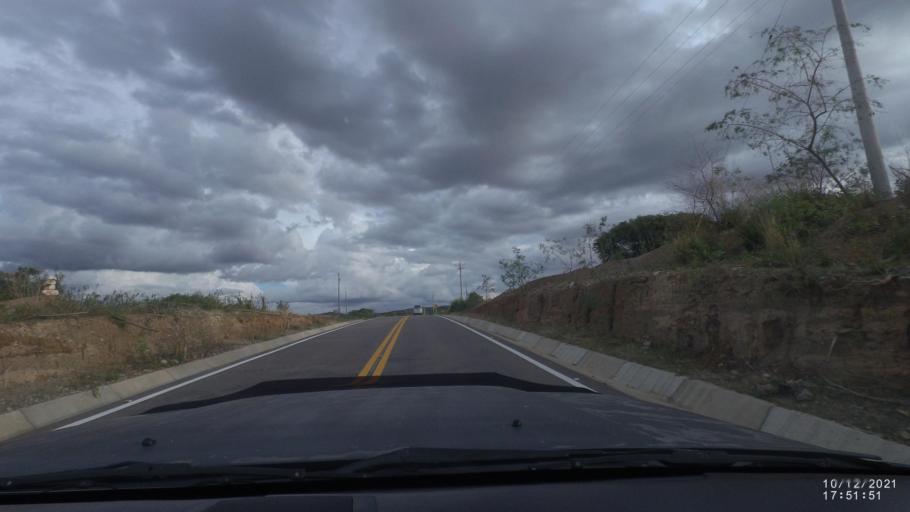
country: BO
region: Cochabamba
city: Cliza
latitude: -17.6805
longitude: -65.9558
